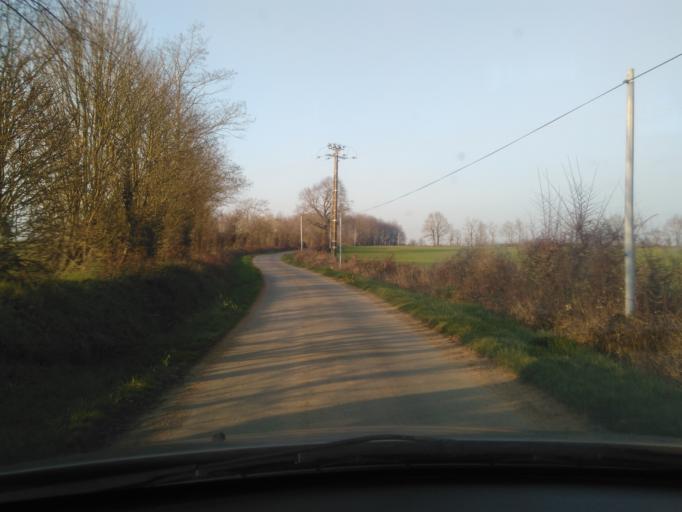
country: FR
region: Pays de la Loire
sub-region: Departement de la Vendee
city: Chantonnay
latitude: 46.6672
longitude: -1.0315
